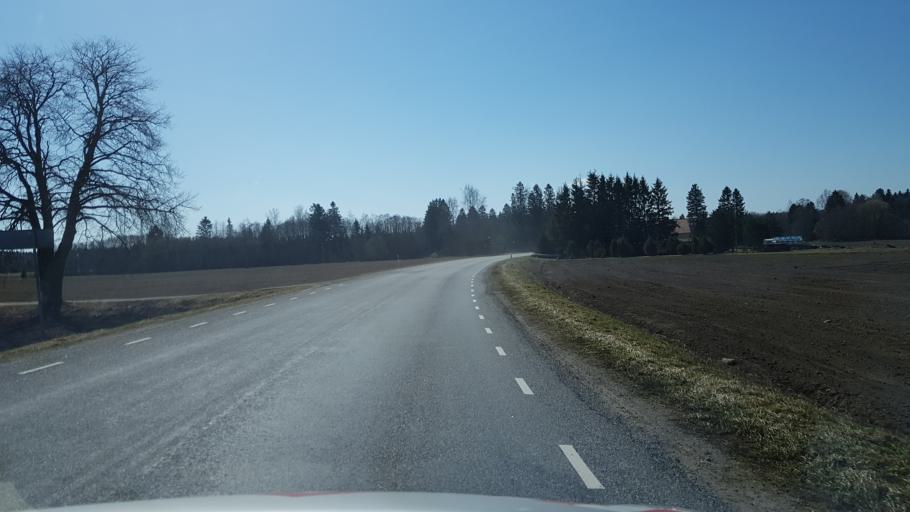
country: EE
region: Ida-Virumaa
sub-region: Kohtla-Nomme vald
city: Kohtla-Nomme
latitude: 59.3043
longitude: 27.2379
